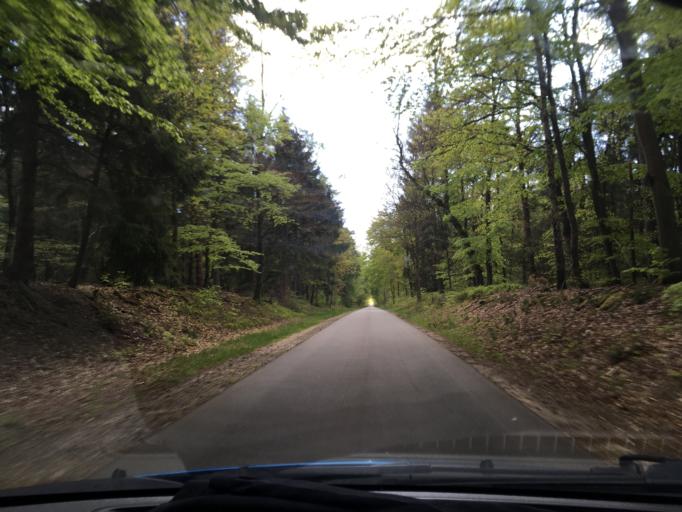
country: DE
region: Lower Saxony
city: Nahrendorf
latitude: 53.1350
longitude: 10.8003
